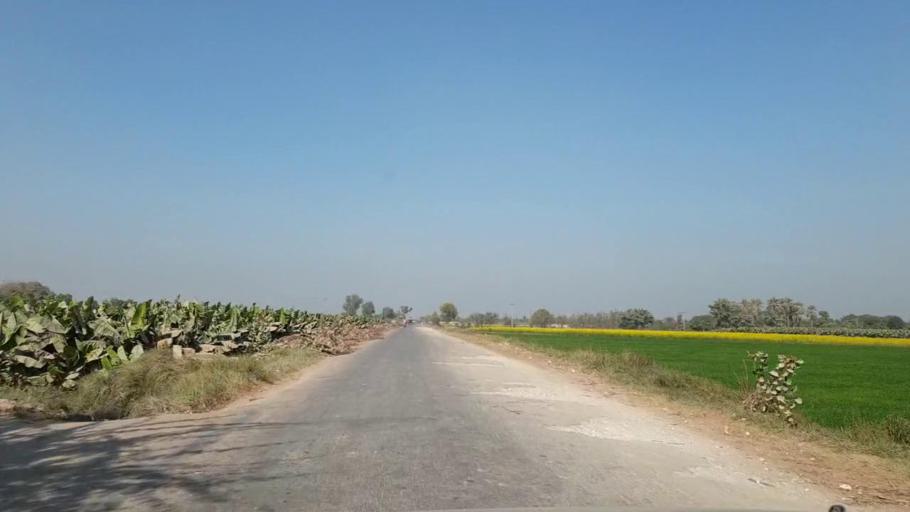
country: PK
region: Sindh
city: Tando Adam
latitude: 25.6439
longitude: 68.5936
